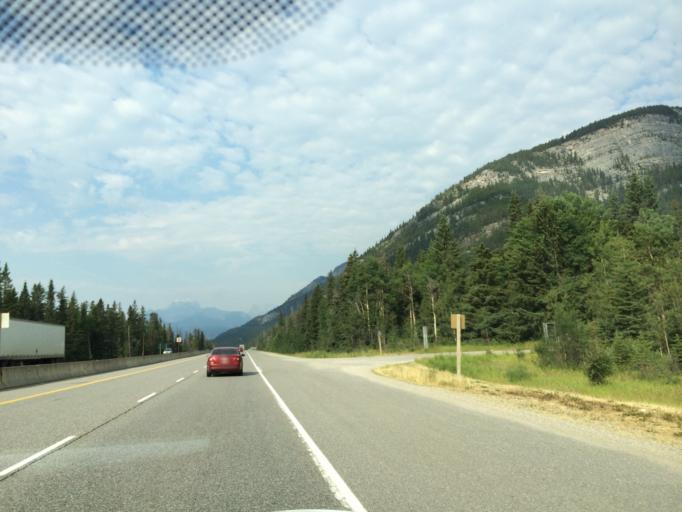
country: CA
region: Alberta
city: Banff
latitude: 51.1952
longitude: -115.5565
